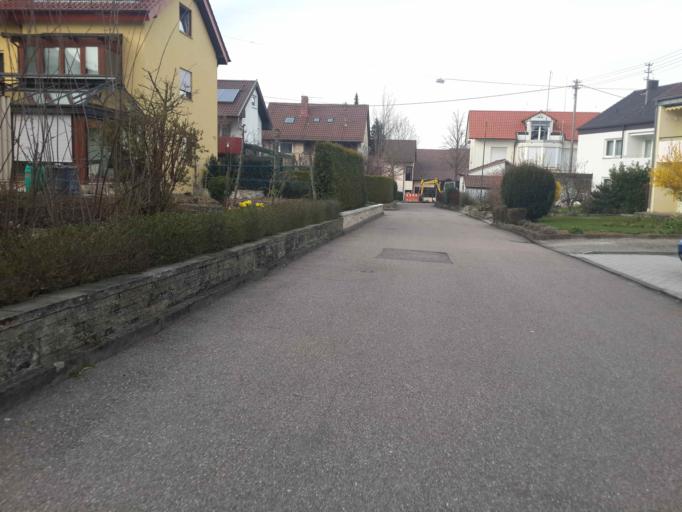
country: DE
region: Baden-Wuerttemberg
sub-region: Regierungsbezirk Stuttgart
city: Nordheim
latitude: 49.1063
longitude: 9.1242
